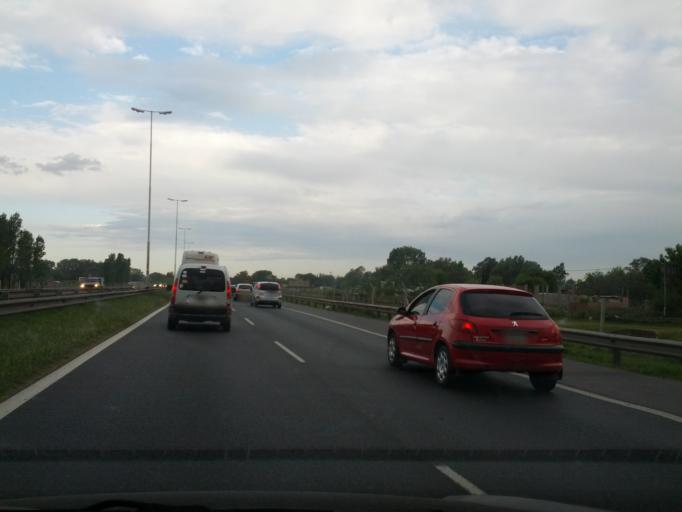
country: AR
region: Buenos Aires
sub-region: Partido de General Rodriguez
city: General Rodriguez
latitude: -34.5993
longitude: -58.9206
